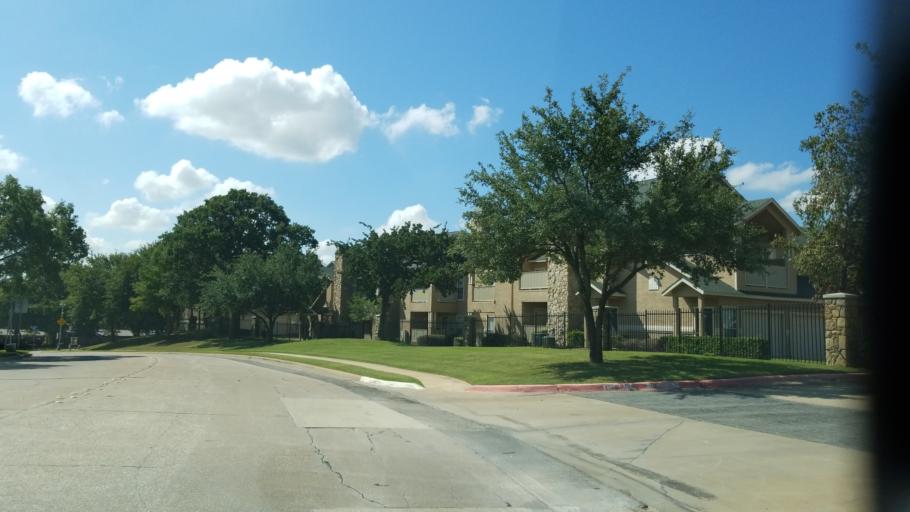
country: US
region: Texas
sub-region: Tarrant County
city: Euless
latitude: 32.8670
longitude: -97.0704
